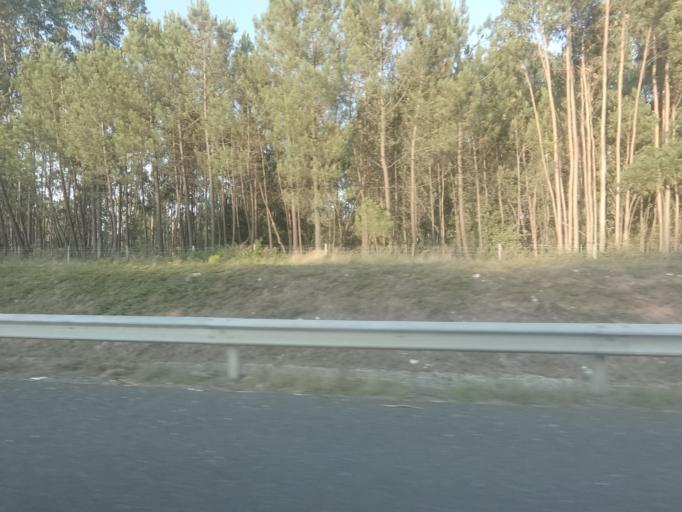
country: PT
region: Santarem
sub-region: Ourem
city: Fatima
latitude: 39.6277
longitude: -8.6971
